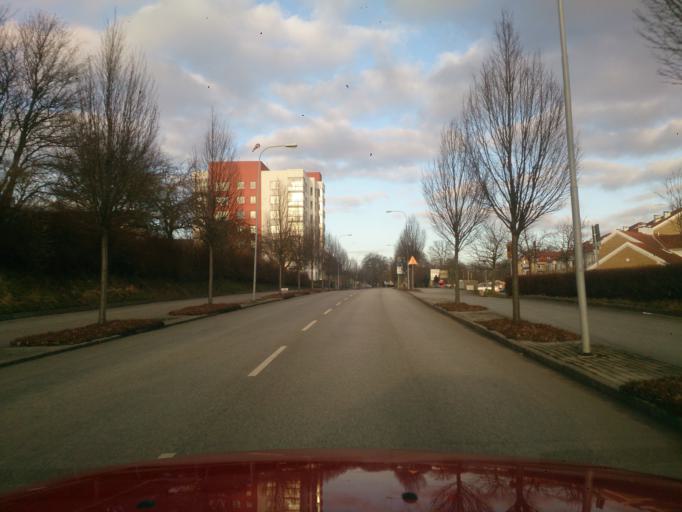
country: SE
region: Skane
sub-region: Ystads Kommun
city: Ystad
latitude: 55.4270
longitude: 13.8056
